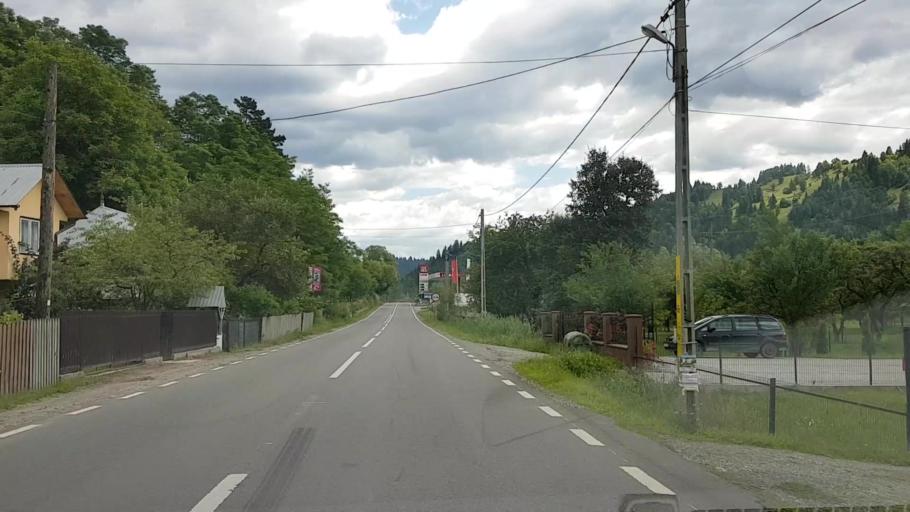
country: RO
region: Neamt
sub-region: Comuna Farcasa
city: Farcasa
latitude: 47.1609
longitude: 25.8200
